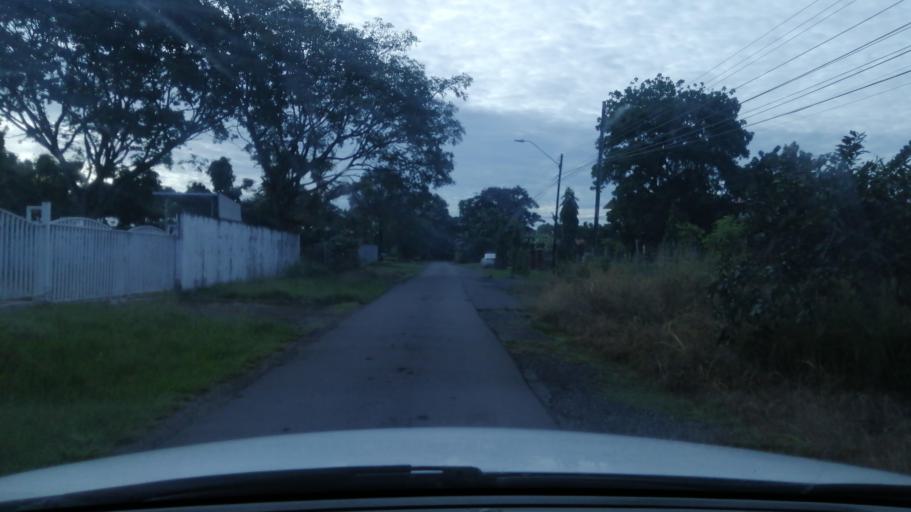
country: PA
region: Chiriqui
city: Mata del Nance
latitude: 8.4551
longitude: -82.4206
